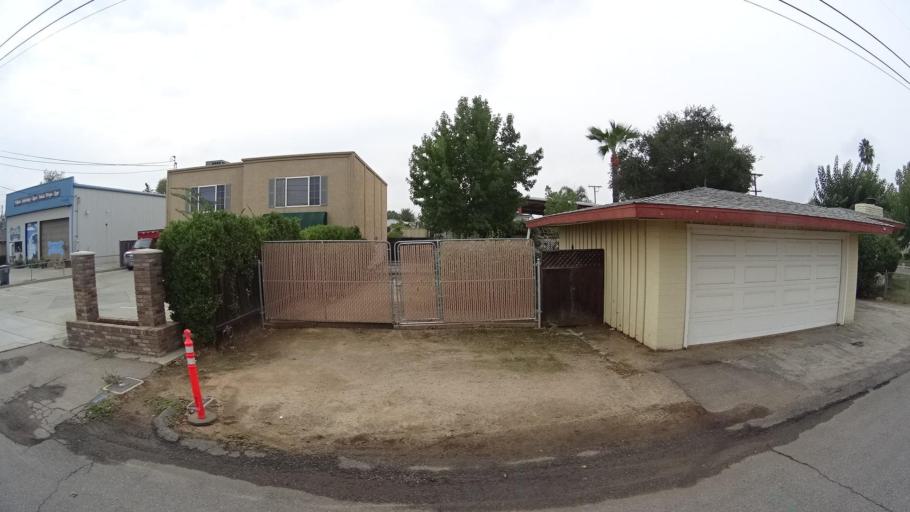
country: US
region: California
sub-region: San Diego County
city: Ramona
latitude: 33.0378
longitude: -116.8739
